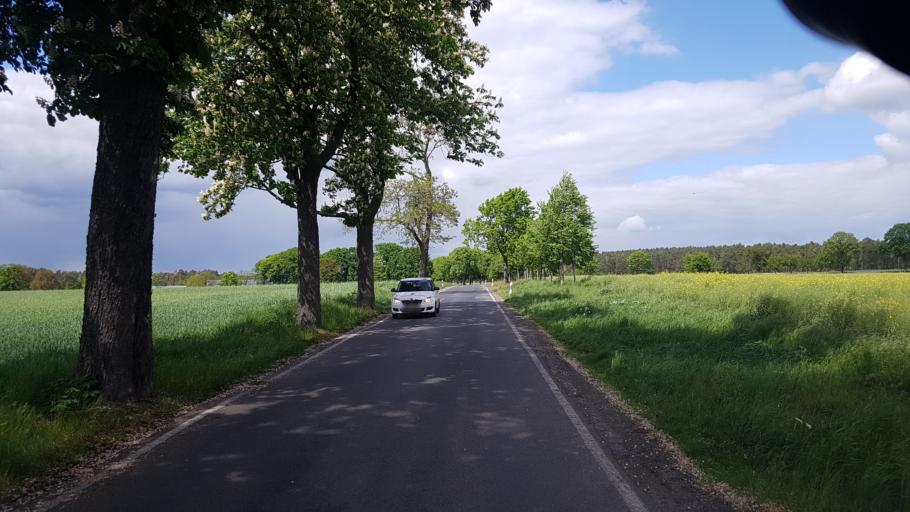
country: DE
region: Brandenburg
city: Bronkow
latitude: 51.6529
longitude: 13.9226
